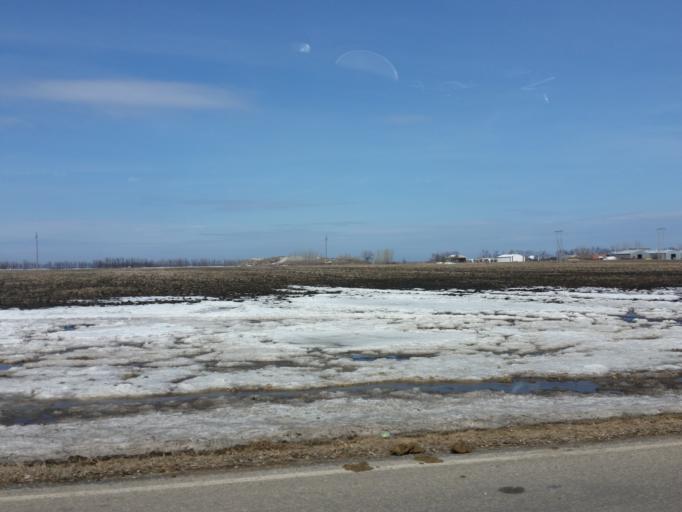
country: US
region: North Dakota
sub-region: Walsh County
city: Grafton
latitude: 48.4268
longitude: -97.4083
